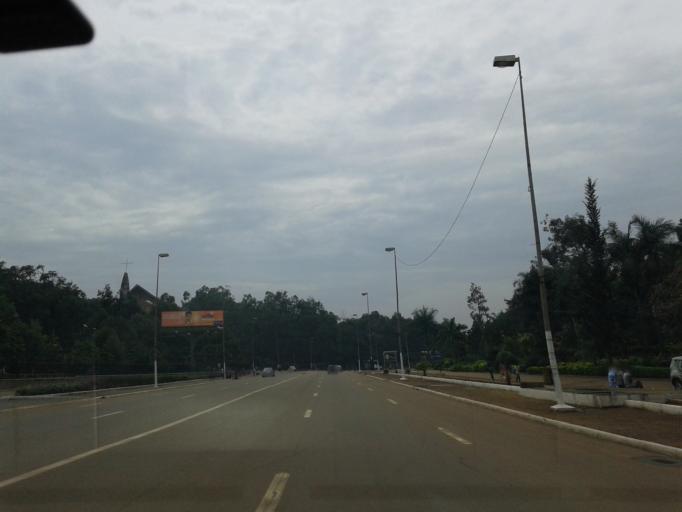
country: CM
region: Centre
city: Yaounde
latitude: 3.8676
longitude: 11.5148
